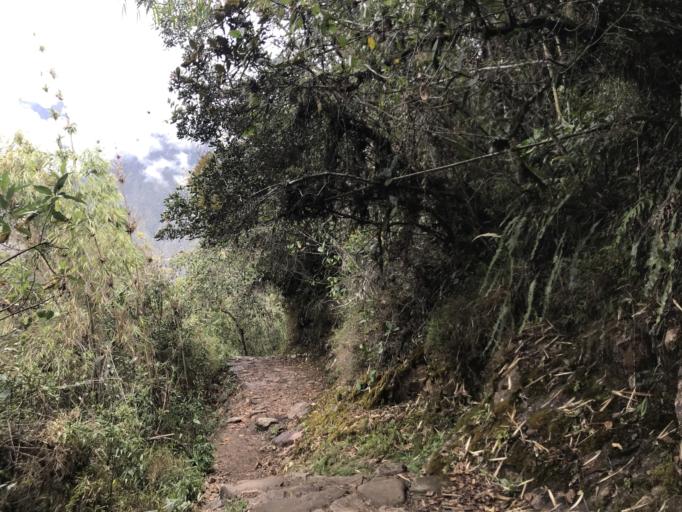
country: PE
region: Cusco
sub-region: Provincia de La Convencion
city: Santa Teresa
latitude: -13.1706
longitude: -72.5338
